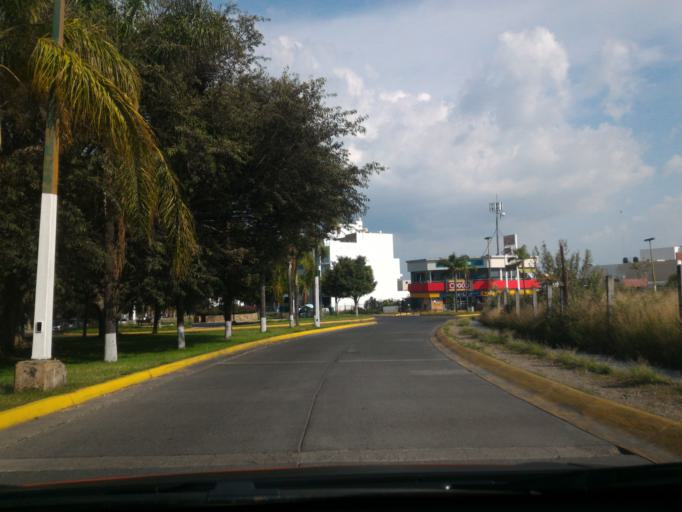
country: MX
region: Jalisco
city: Guadalajara
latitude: 20.6640
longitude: -103.4456
